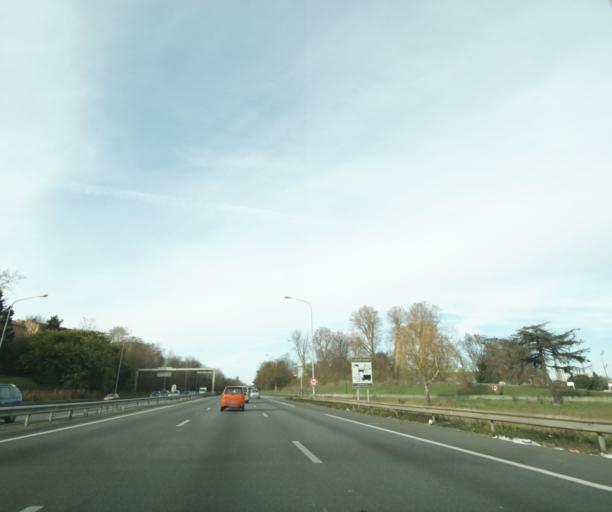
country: FR
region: Midi-Pyrenees
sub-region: Departement de la Haute-Garonne
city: Toulouse
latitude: 43.5862
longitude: 1.4020
